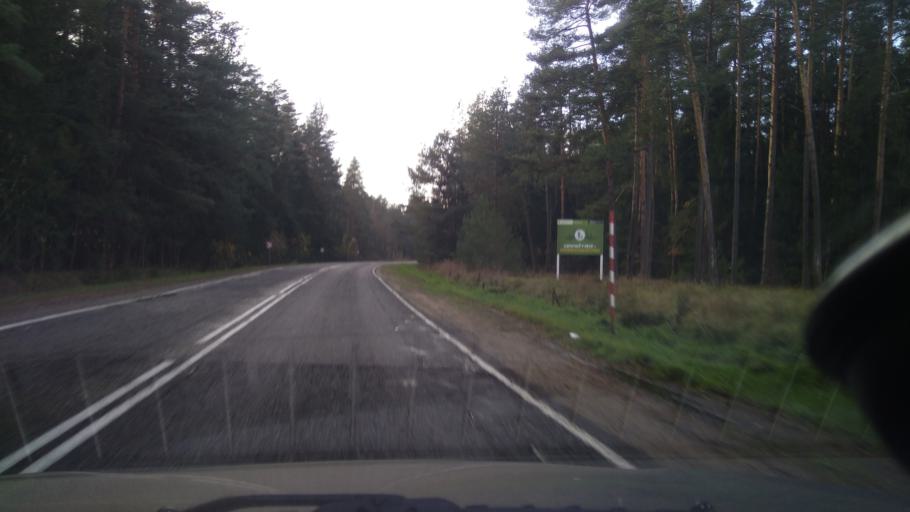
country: BY
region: Minsk
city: Slutsk
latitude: 53.2233
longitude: 27.6043
